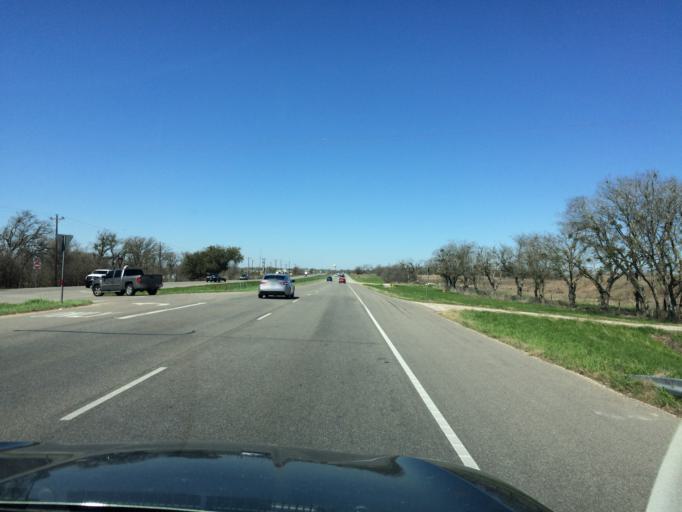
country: US
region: Texas
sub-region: Travis County
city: Garfield
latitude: 30.1797
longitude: -97.5354
